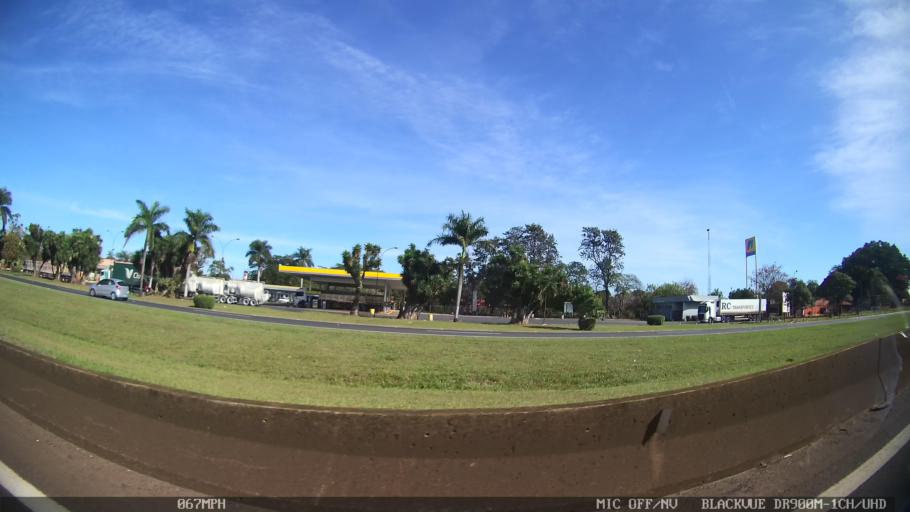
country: BR
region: Sao Paulo
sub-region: Leme
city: Leme
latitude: -22.2248
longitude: -47.3916
